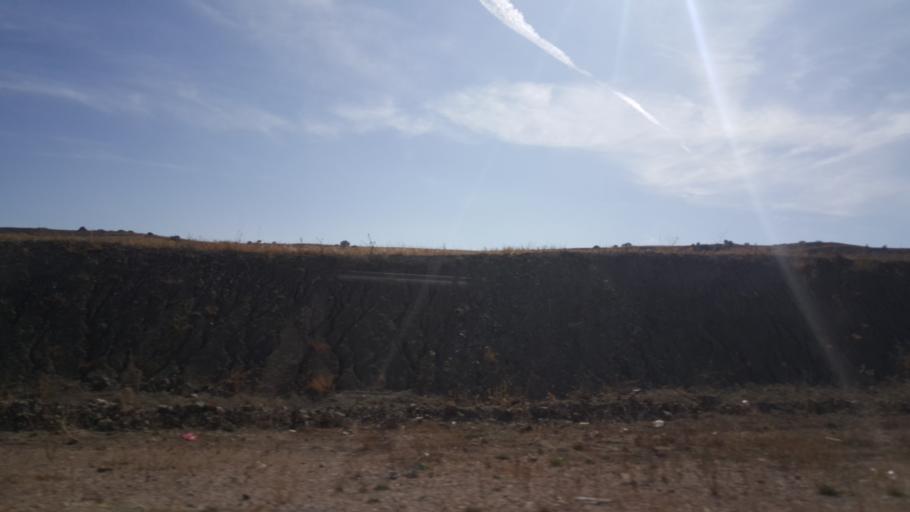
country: TR
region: Ankara
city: Haymana
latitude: 39.4258
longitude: 32.5644
